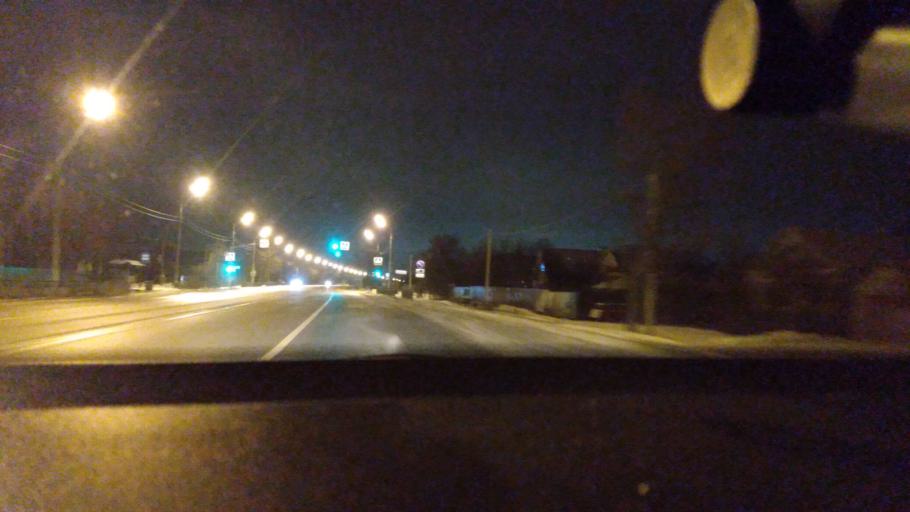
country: RU
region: Moskovskaya
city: Bronnitsy
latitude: 55.3974
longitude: 38.3182
